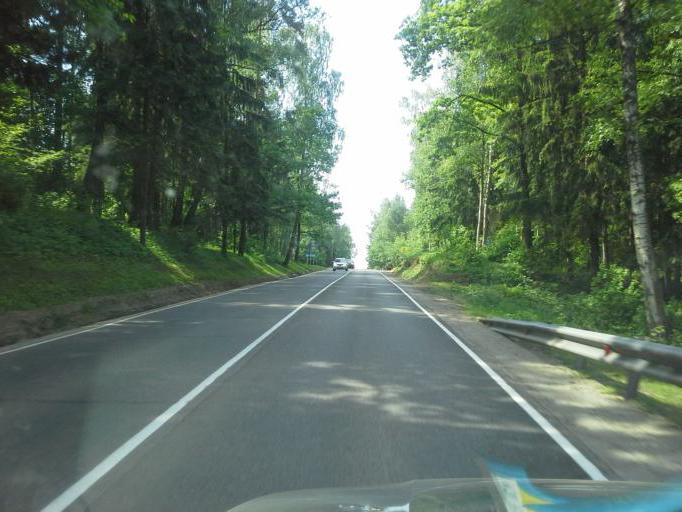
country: RU
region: Moskovskaya
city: Gorki Vtoryye
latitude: 55.7106
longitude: 37.2074
